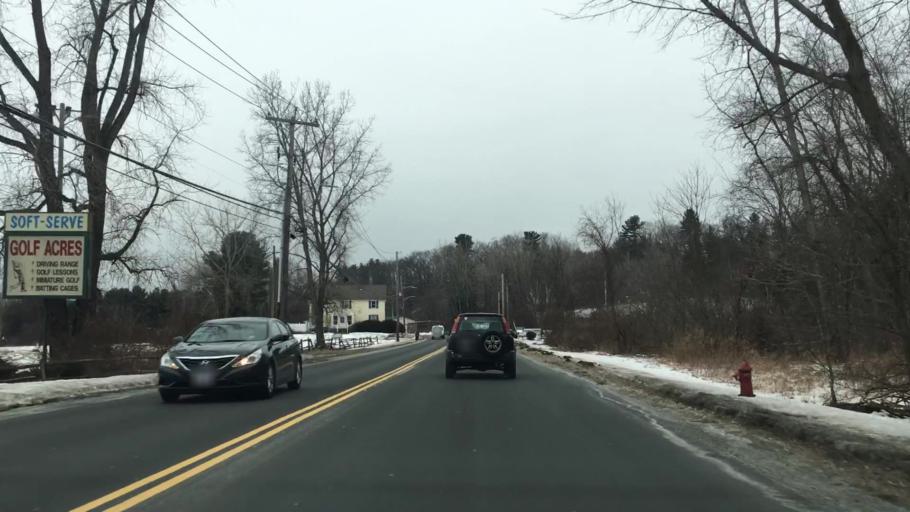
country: US
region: Massachusetts
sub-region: Hampden County
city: Westfield
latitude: 42.1202
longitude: -72.7156
